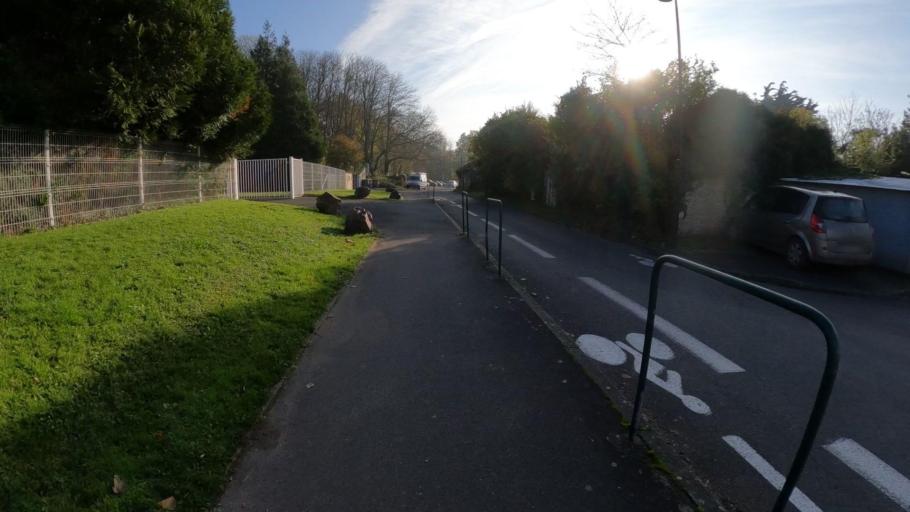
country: FR
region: Lower Normandy
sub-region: Departement du Calvados
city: Epron
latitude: 49.2130
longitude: -0.3409
